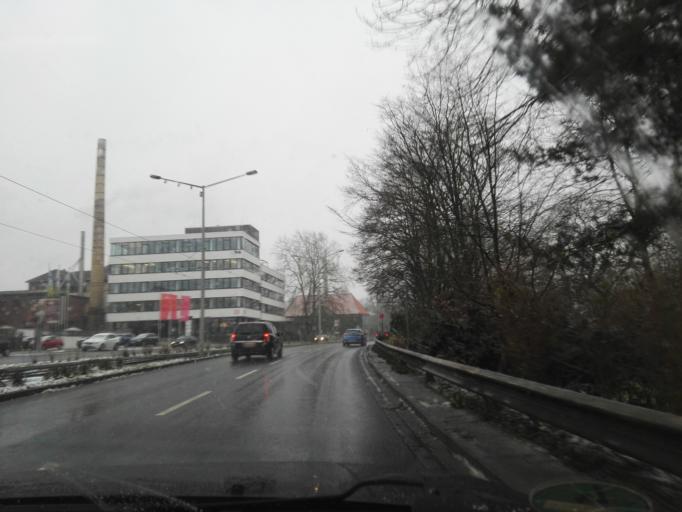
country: DE
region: Lower Saxony
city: Braunschweig
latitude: 52.2497
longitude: 10.5295
